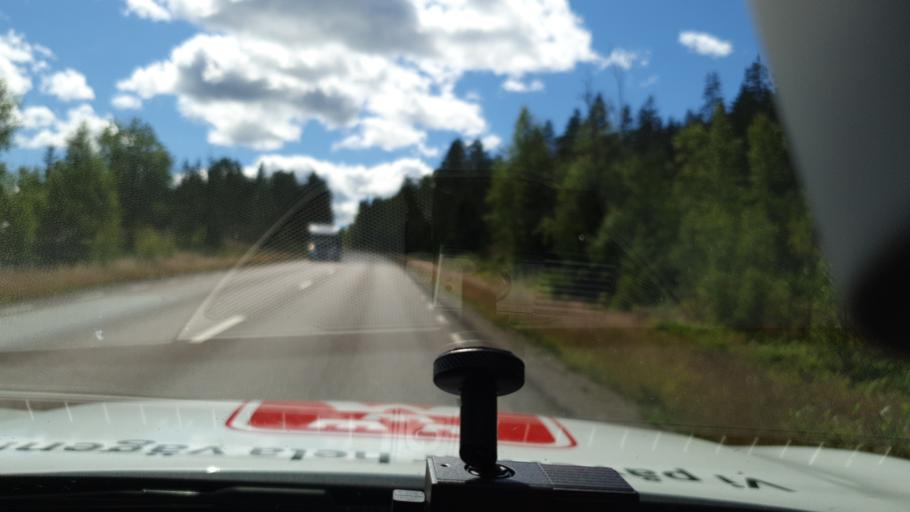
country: SE
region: Vaermland
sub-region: Sunne Kommun
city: Sunne
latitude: 59.7055
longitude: 13.1061
